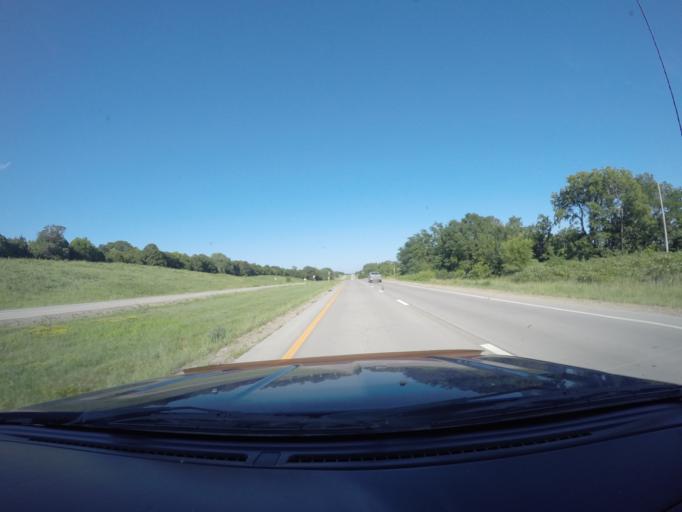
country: US
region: Kansas
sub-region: Shawnee County
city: Topeka
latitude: 39.0877
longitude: -95.5177
